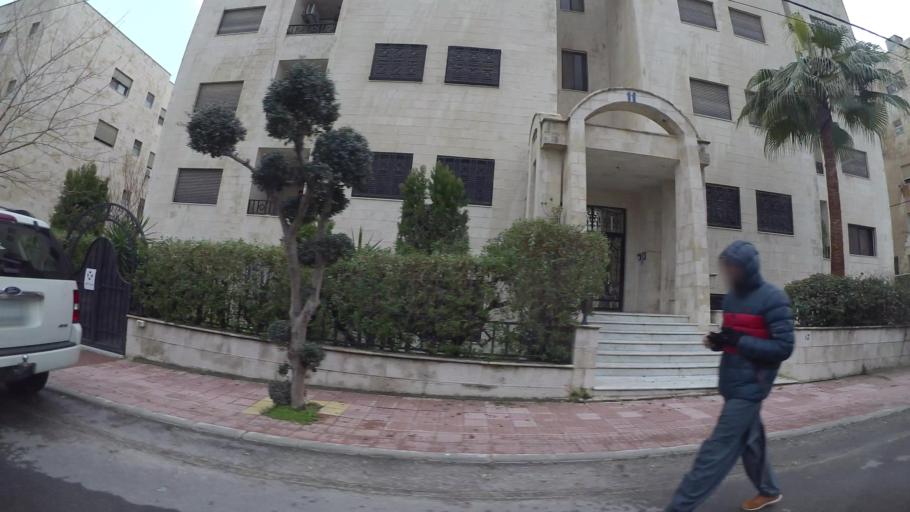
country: JO
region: Amman
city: Wadi as Sir
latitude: 31.9498
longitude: 35.8772
